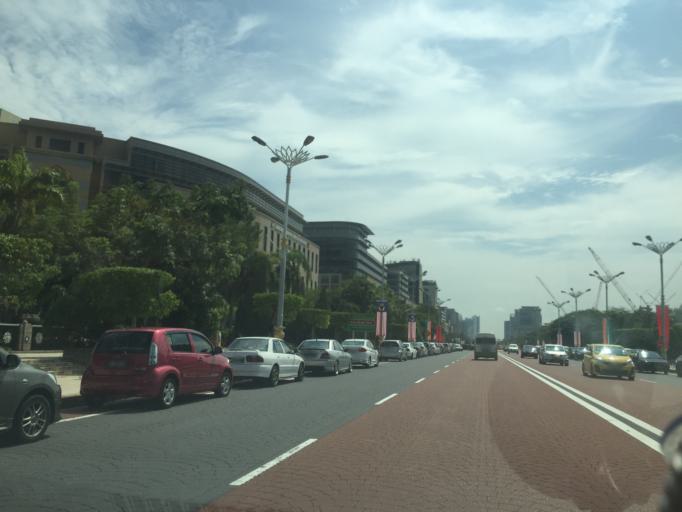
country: MY
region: Putrajaya
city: Putrajaya
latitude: 2.9309
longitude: 101.6897
